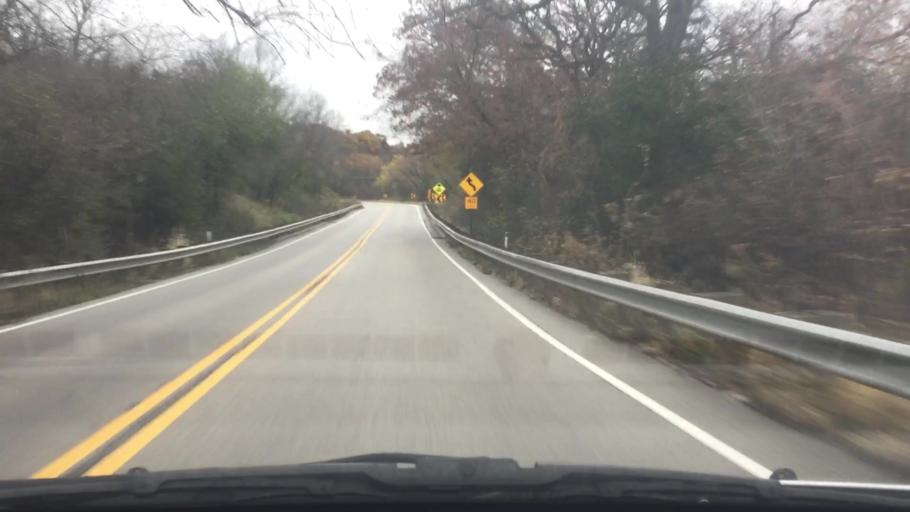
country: US
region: Wisconsin
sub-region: Waukesha County
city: Eagle
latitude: 42.9030
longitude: -88.4737
